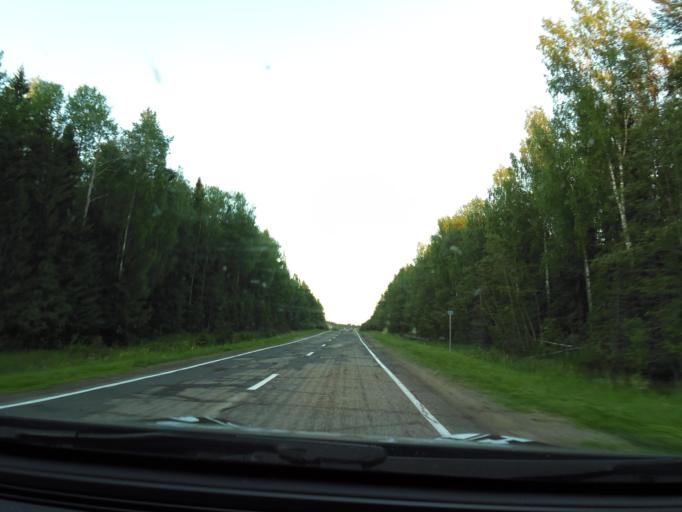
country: RU
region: Jaroslavl
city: Lyubim
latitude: 58.3566
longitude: 40.6049
